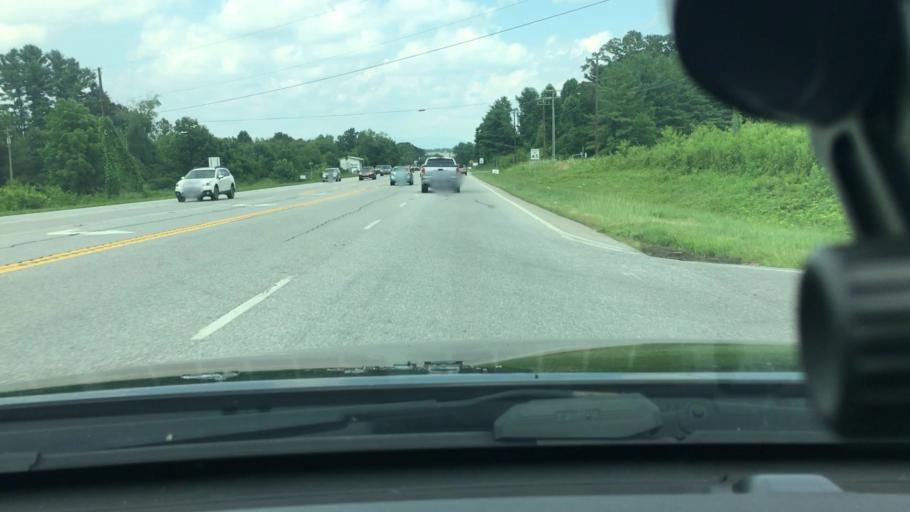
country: US
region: North Carolina
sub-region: Henderson County
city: Mills River
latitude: 35.3831
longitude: -82.5706
